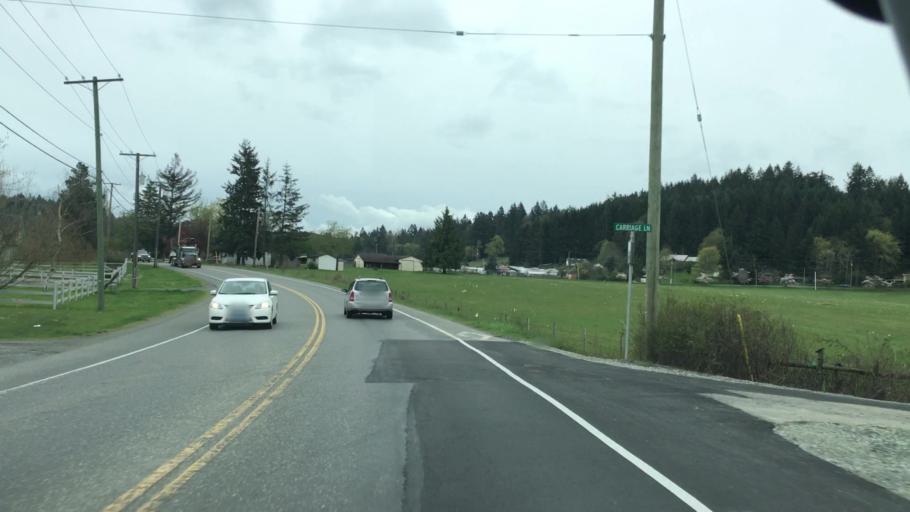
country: CA
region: British Columbia
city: North Saanich
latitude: 48.5690
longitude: -123.4413
